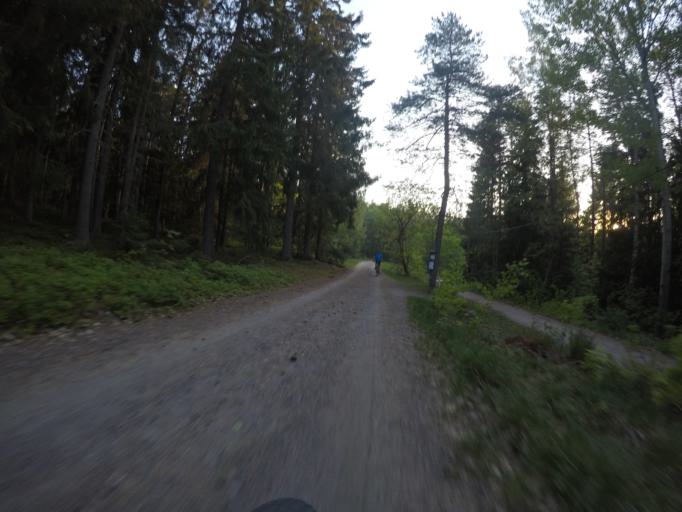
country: SE
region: Soedermanland
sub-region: Eskilstuna Kommun
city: Eskilstuna
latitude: 59.3459
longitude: 16.5118
